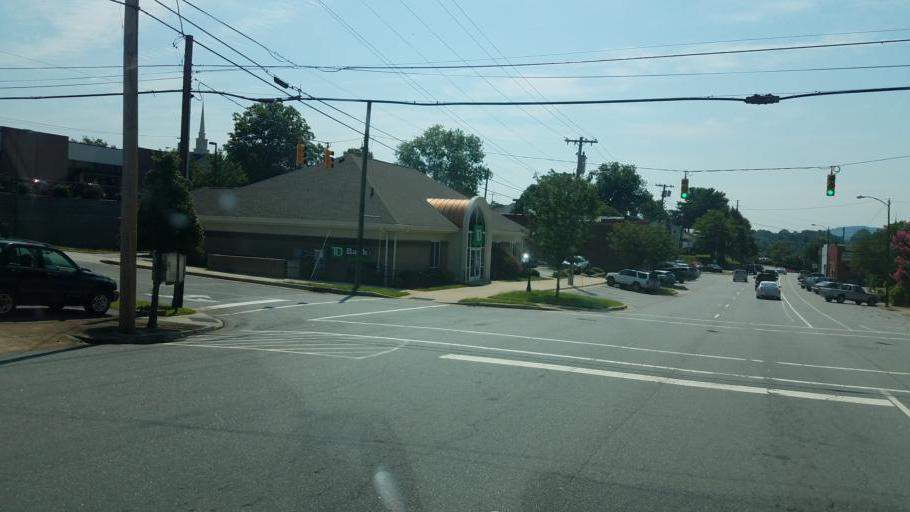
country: US
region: North Carolina
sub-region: Burke County
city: Morganton
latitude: 35.7434
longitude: -81.6849
